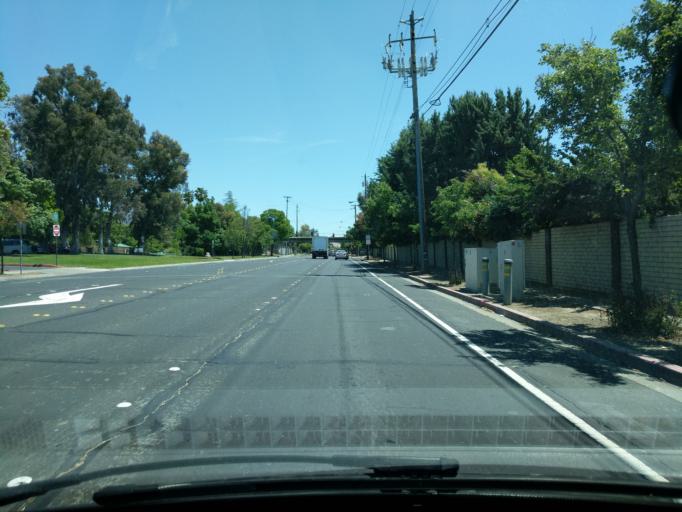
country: US
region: California
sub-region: Contra Costa County
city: Pleasant Hill
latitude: 37.9446
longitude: -122.0305
